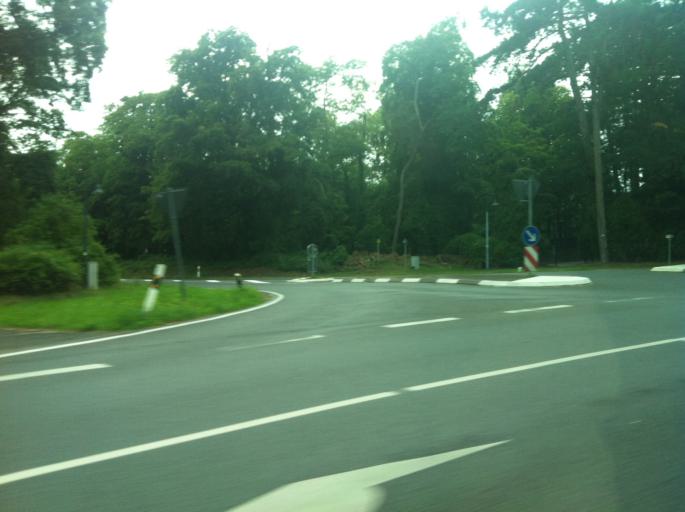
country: DE
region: Rheinland-Pfalz
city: Budenheim
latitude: 50.0084
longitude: 8.1789
